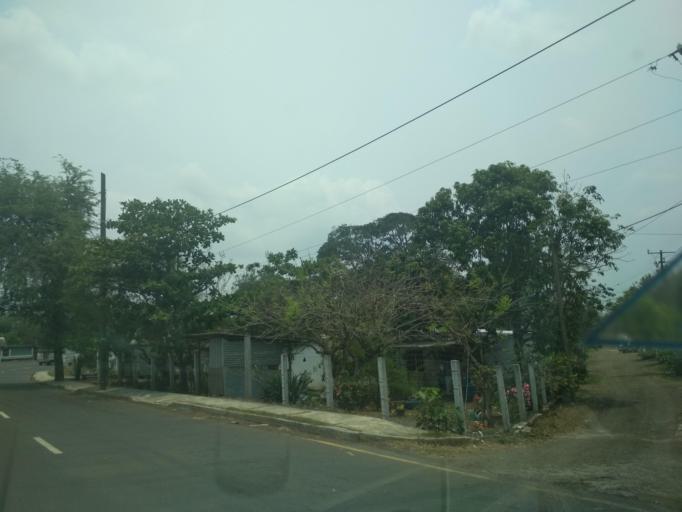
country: MX
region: Veracruz
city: Manlio Fabio Altamirano
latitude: 19.1332
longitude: -96.2978
